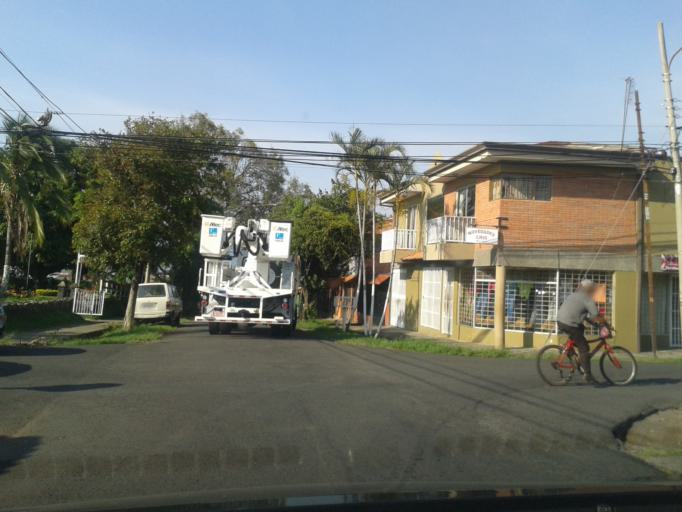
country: CR
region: Heredia
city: Llorente
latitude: 10.0022
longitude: -84.1512
